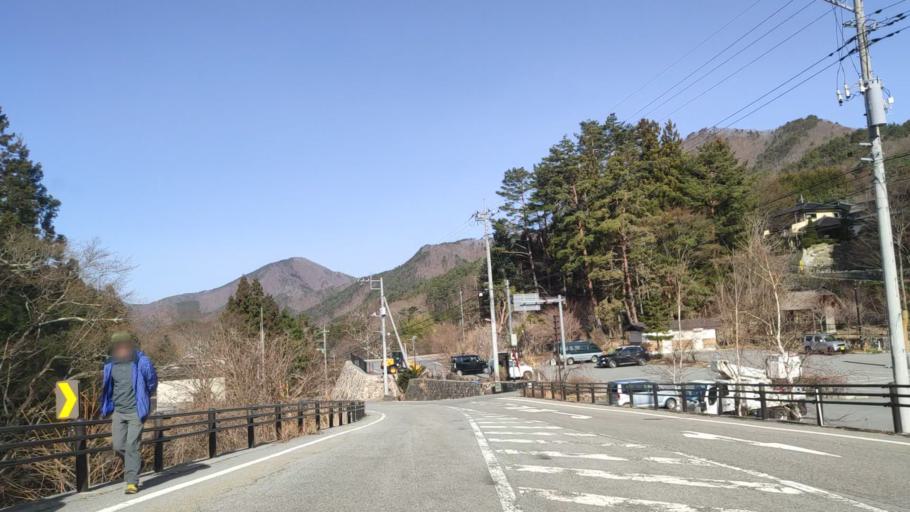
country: JP
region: Yamanashi
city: Fujikawaguchiko
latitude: 35.5523
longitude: 138.6887
